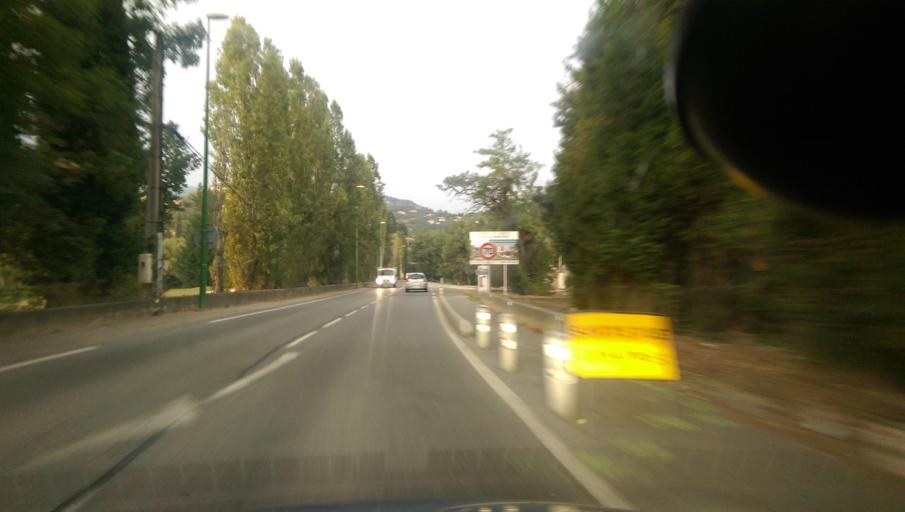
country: FR
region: Provence-Alpes-Cote d'Azur
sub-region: Departement des Alpes-Maritimes
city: Chateauneuf-Grasse
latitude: 43.6654
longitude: 6.9855
